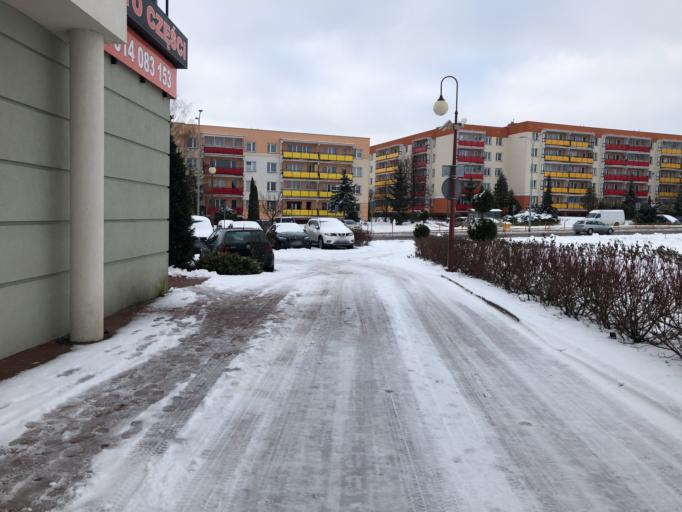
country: PL
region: Podlasie
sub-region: Lomza
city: Lomza
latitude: 53.1563
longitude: 22.0753
